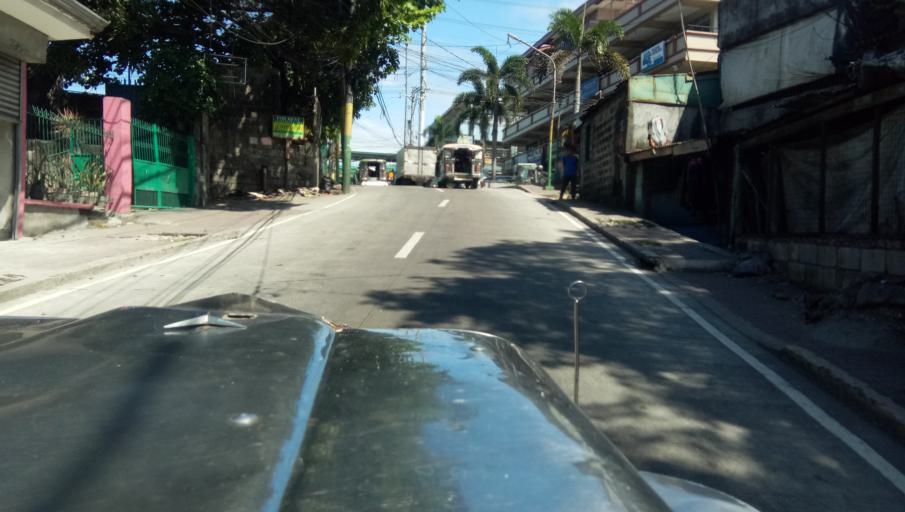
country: PH
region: Calabarzon
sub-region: Province of Cavite
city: Dasmarinas
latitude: 14.3265
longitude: 120.9391
